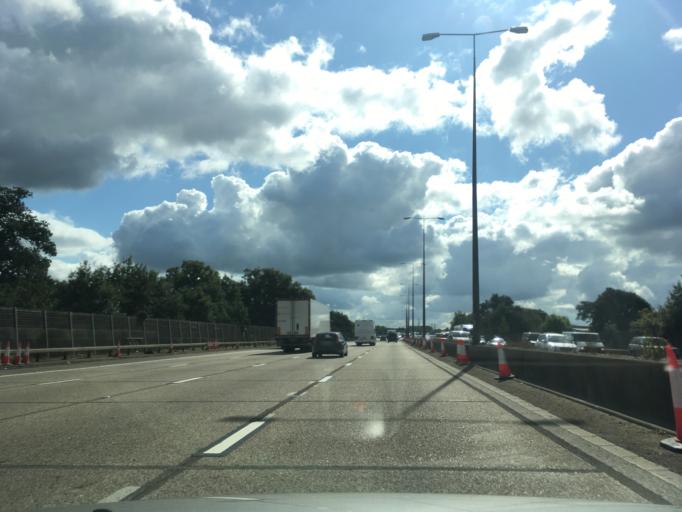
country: GB
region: England
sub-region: Surrey
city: Addlestone
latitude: 51.3600
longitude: -0.4969
